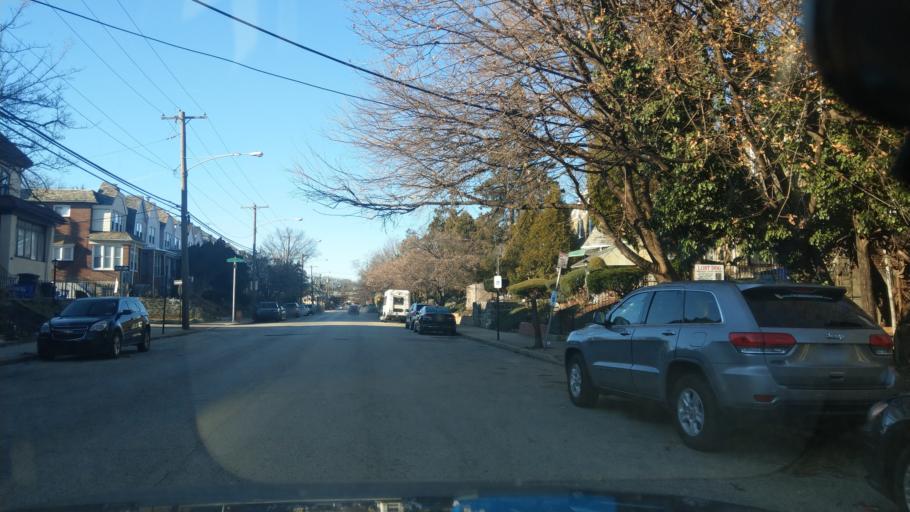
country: US
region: Pennsylvania
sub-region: Montgomery County
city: Wyncote
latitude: 40.0416
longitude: -75.1523
